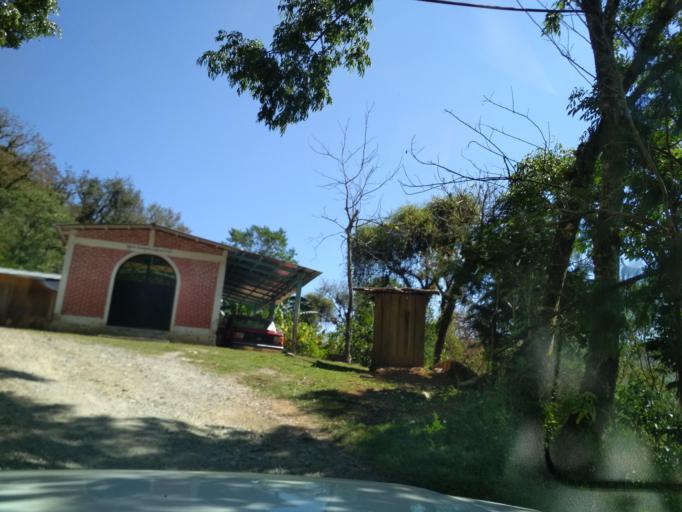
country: MX
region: Veracruz
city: Tequila
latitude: 18.7525
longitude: -97.0943
